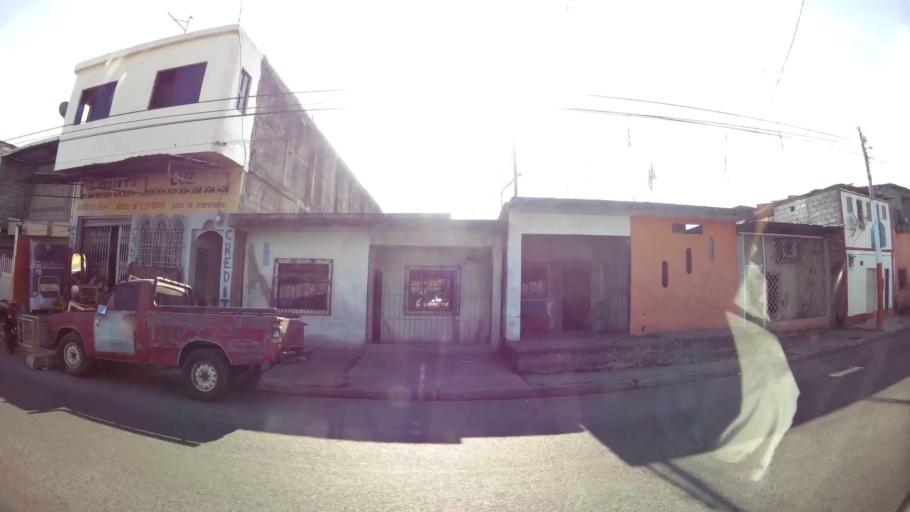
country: EC
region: Guayas
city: Guayaquil
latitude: -2.2210
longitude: -79.9259
